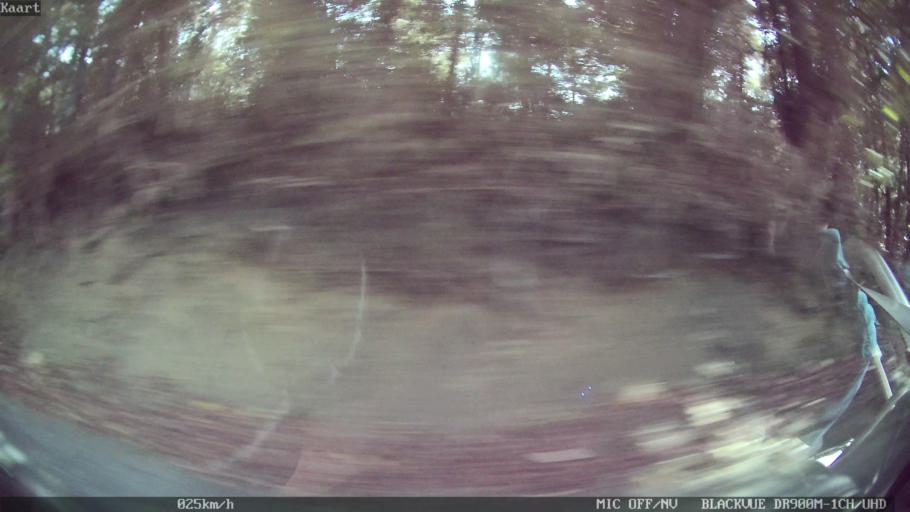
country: ID
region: Bali
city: Banjar Kedisan
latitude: -8.2888
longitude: 115.3785
